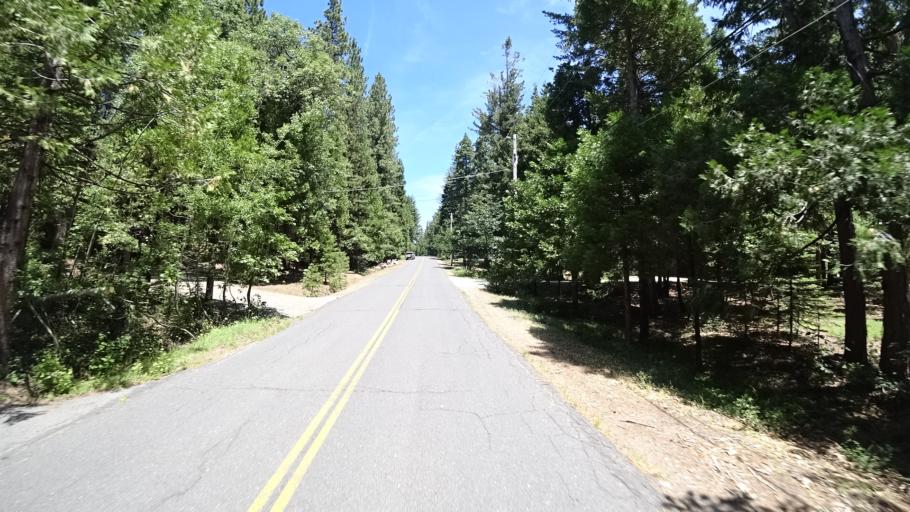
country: US
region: California
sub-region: Calaveras County
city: Arnold
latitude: 38.3057
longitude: -120.2620
